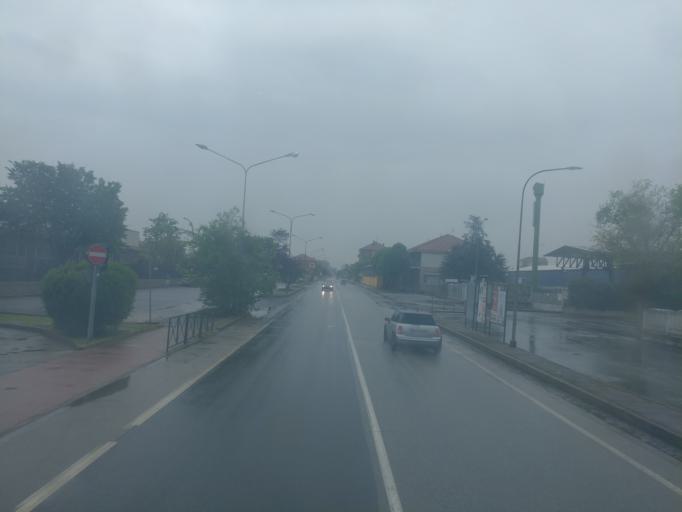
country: IT
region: Piedmont
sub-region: Provincia di Torino
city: La Loggia
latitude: 44.9470
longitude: 7.6695
